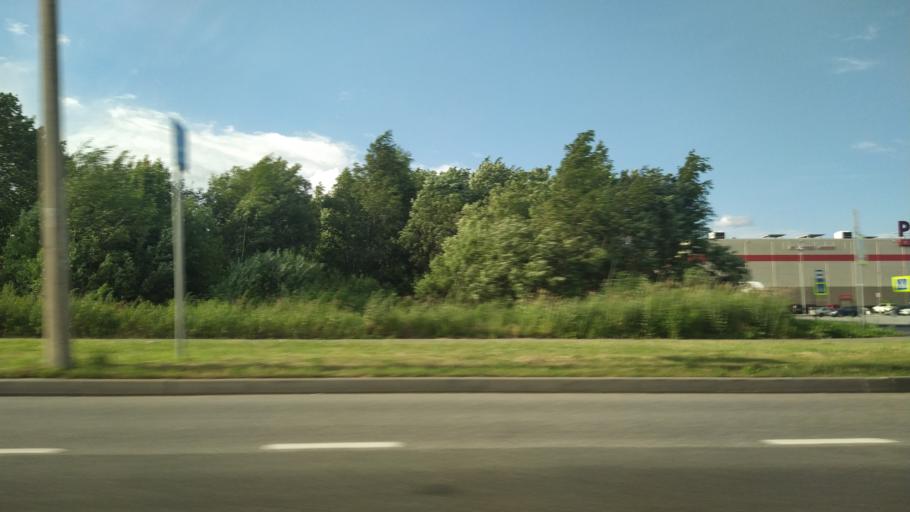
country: RU
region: St.-Petersburg
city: Krasnogvargeisky
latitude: 59.9885
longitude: 30.4635
